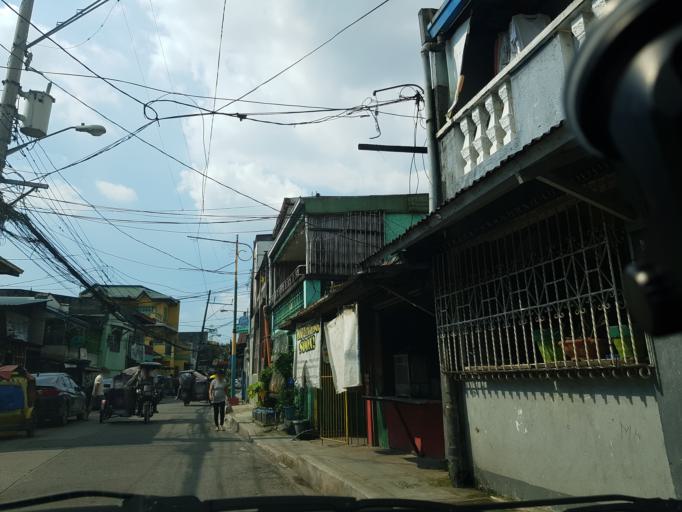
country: PH
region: Calabarzon
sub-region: Province of Rizal
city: Pateros
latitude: 14.5576
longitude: 121.0905
